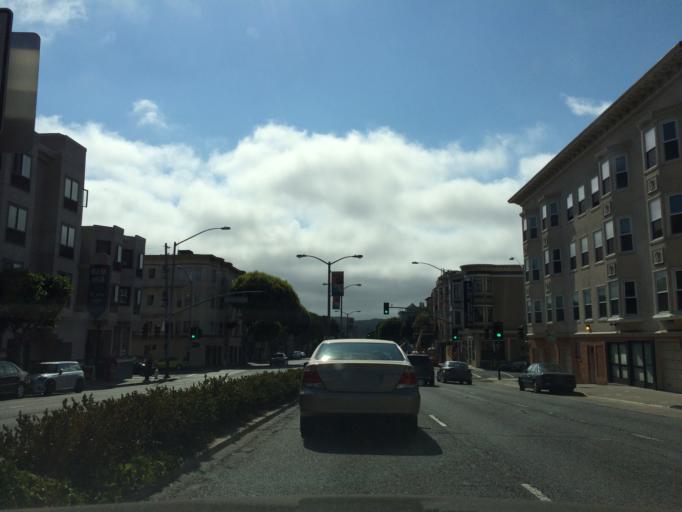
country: US
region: California
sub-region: San Francisco County
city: San Francisco
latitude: 37.8010
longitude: -122.4272
